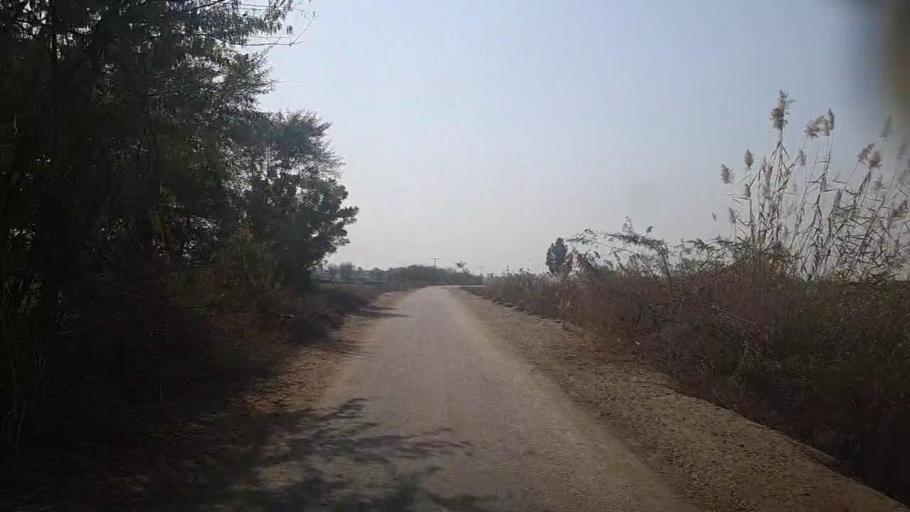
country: PK
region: Sindh
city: Kot Diji
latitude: 27.4122
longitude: 68.7927
